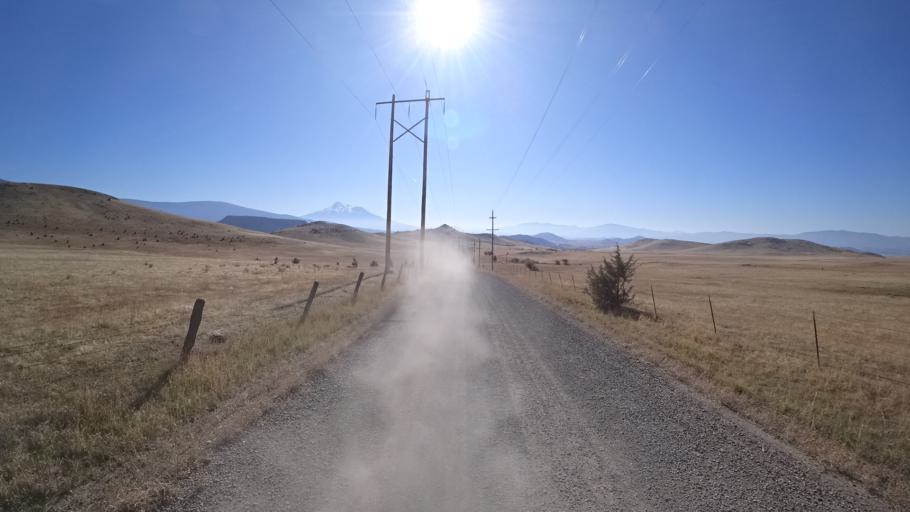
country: US
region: California
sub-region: Siskiyou County
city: Montague
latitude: 41.7612
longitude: -122.3592
